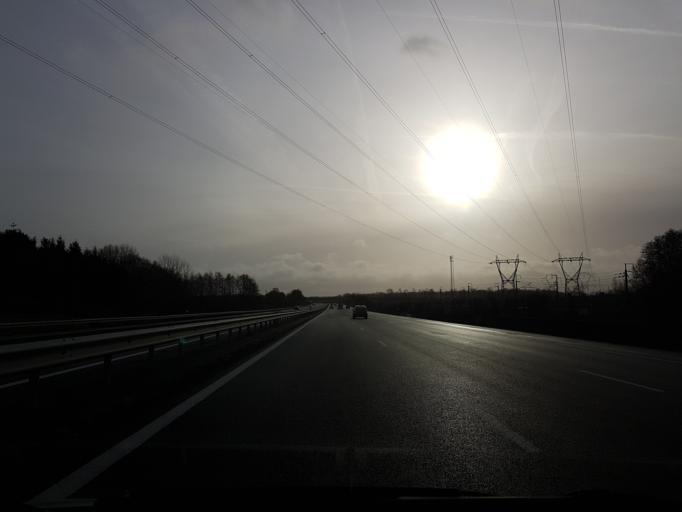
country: FR
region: Ile-de-France
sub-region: Departement de Seine-et-Marne
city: Moisenay
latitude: 48.5515
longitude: 2.7759
